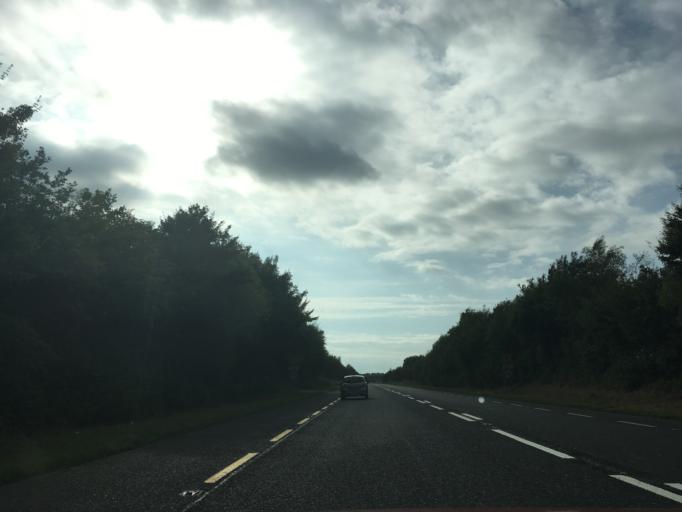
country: IE
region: Leinster
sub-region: Loch Garman
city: Loch Garman
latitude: 52.3475
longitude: -6.6140
